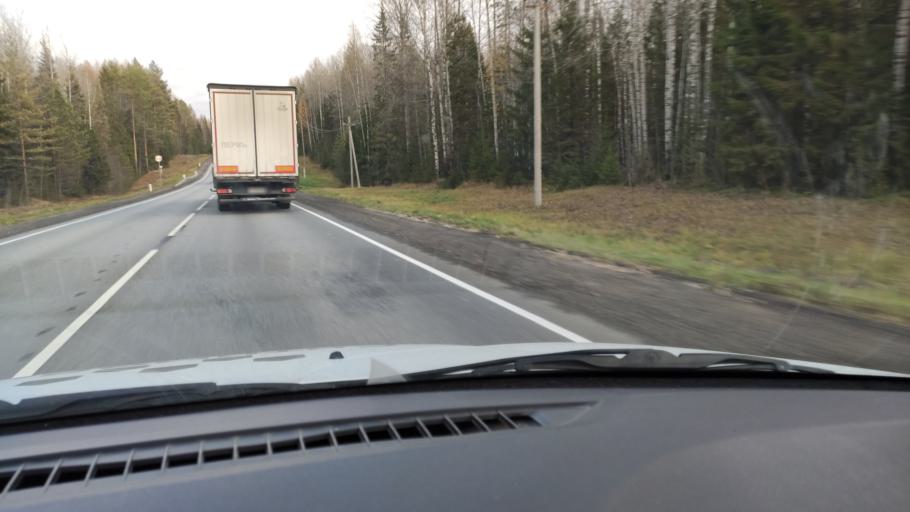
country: RU
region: Kirov
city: Dubrovka
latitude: 58.9136
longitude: 51.1630
